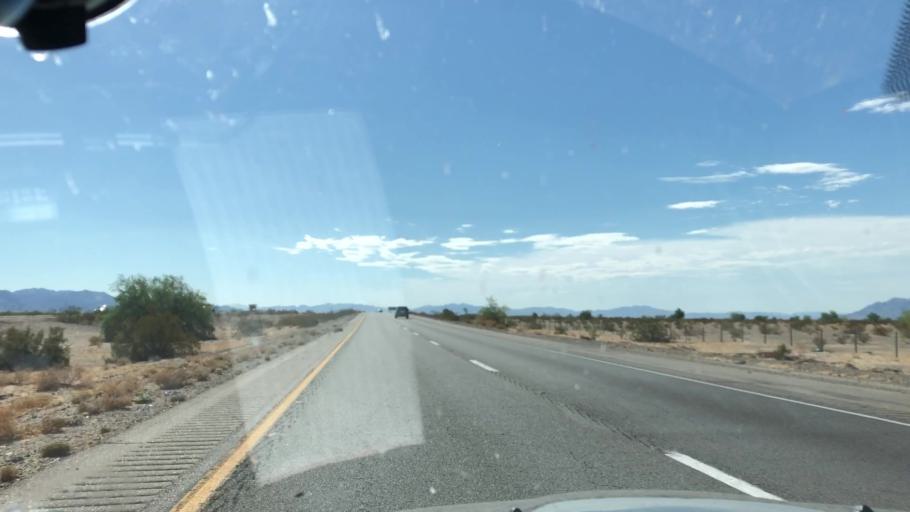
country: US
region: California
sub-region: Riverside County
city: Mesa Verde
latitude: 33.6505
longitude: -115.1347
